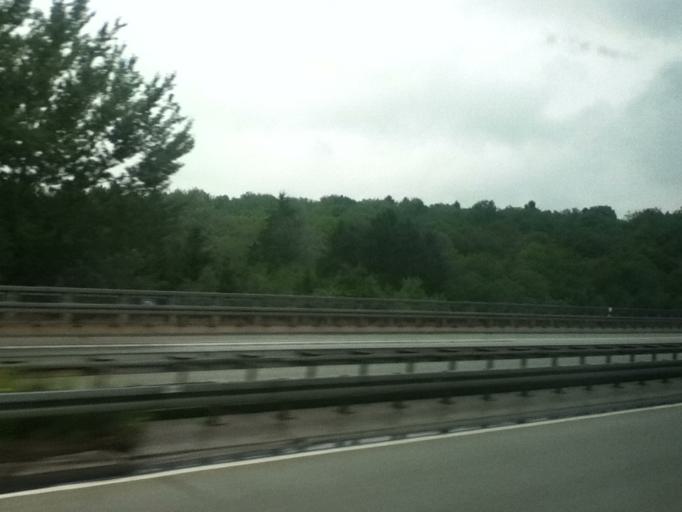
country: DE
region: North Rhine-Westphalia
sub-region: Regierungsbezirk Arnsberg
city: Wilnsdorf
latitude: 50.8266
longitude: 8.0606
